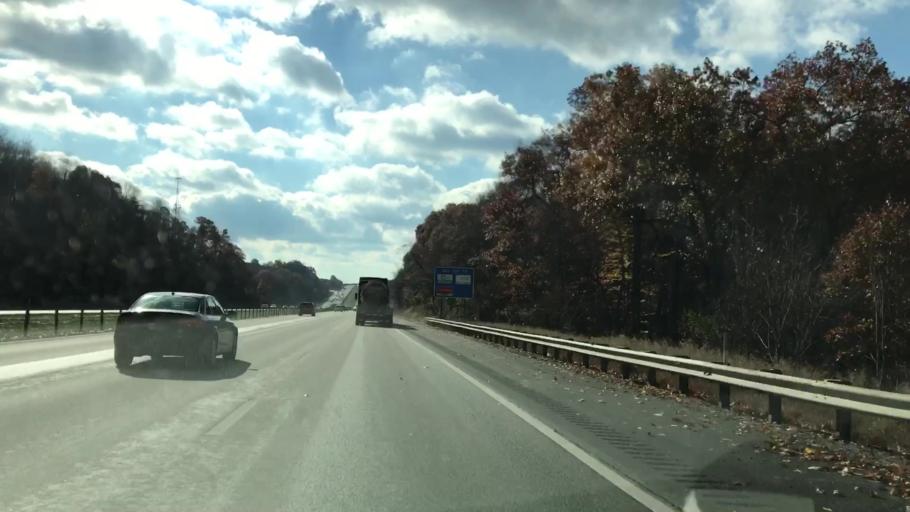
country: US
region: Pennsylvania
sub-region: Allegheny County
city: Bradford Woods
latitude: 40.6304
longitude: -80.0977
